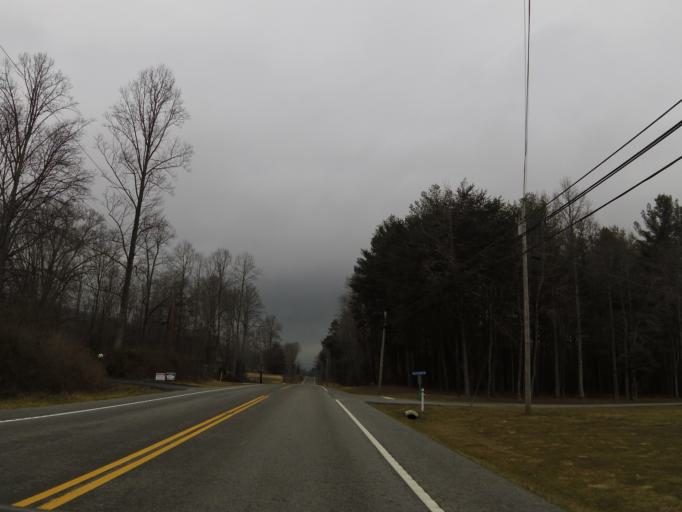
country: US
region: Tennessee
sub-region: Morgan County
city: Wartburg
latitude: 36.0586
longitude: -84.5341
